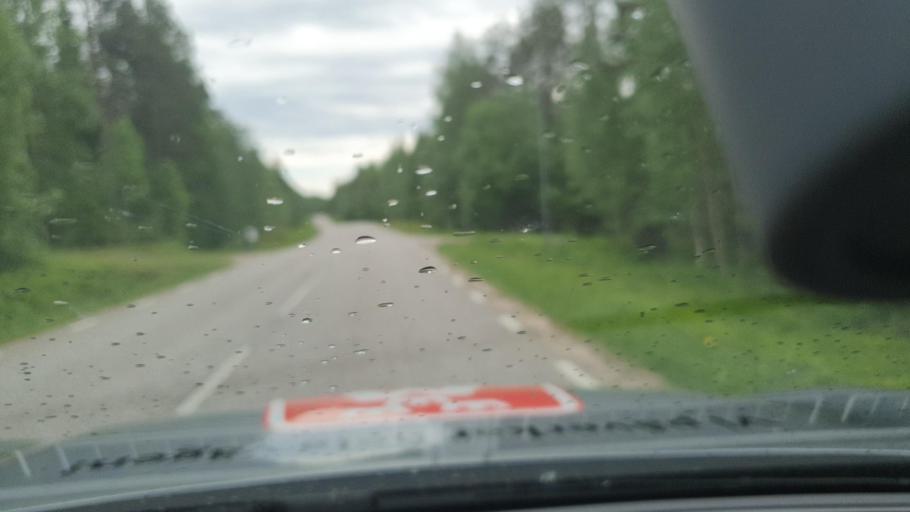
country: SE
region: Norrbotten
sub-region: Kalix Kommun
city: Kalix
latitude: 66.0077
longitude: 23.1435
